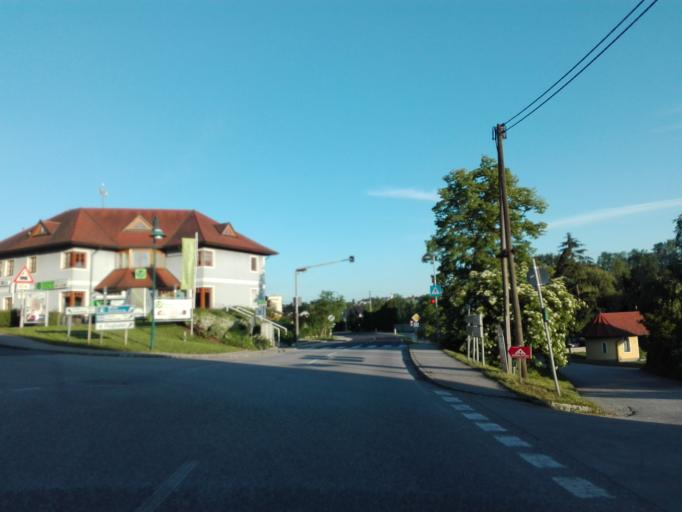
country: AT
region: Upper Austria
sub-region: Politischer Bezirk Urfahr-Umgebung
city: Ottensheim
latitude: 48.2839
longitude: 14.1469
